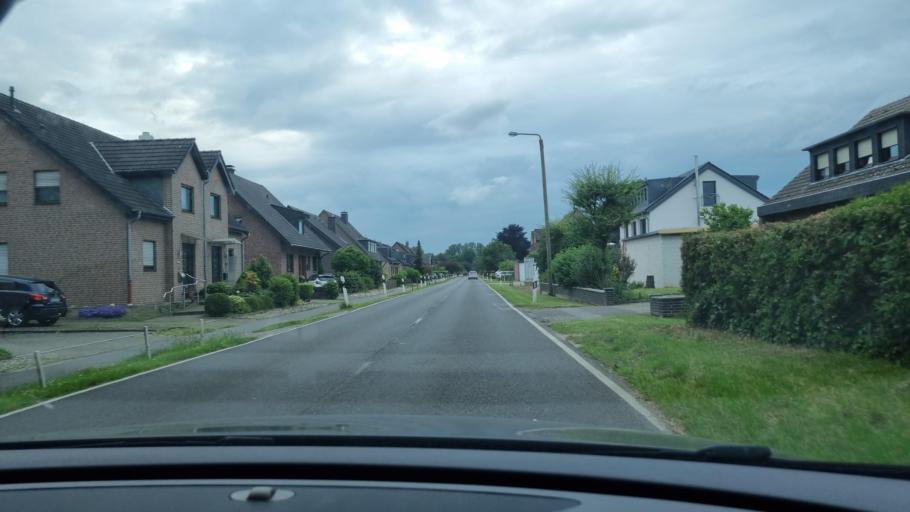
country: DE
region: North Rhine-Westphalia
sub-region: Regierungsbezirk Dusseldorf
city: Voerde
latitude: 51.5831
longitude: 6.6940
